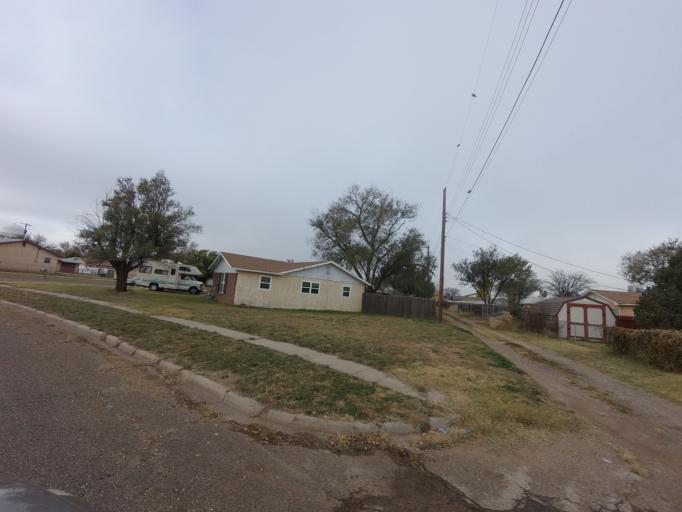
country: US
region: New Mexico
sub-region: Curry County
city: Clovis
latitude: 34.4294
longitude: -103.2255
